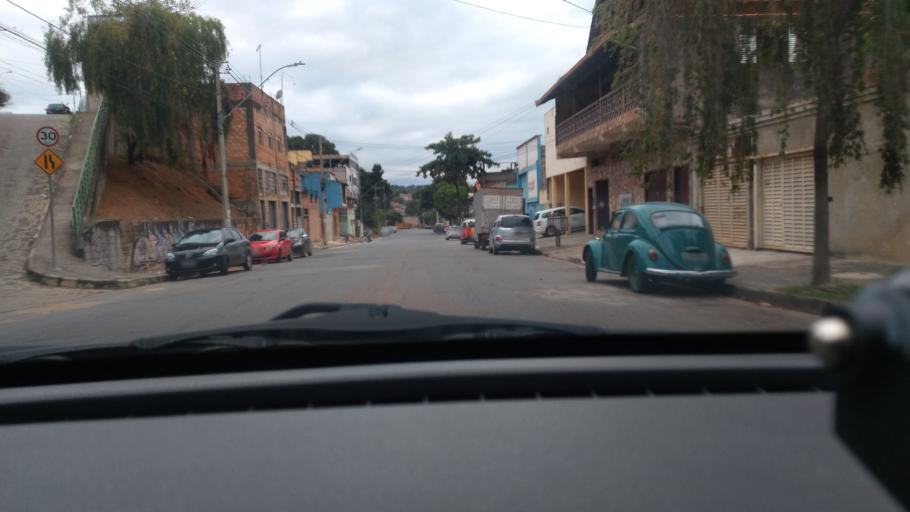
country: BR
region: Minas Gerais
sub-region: Belo Horizonte
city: Belo Horizonte
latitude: -19.8279
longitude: -43.9348
